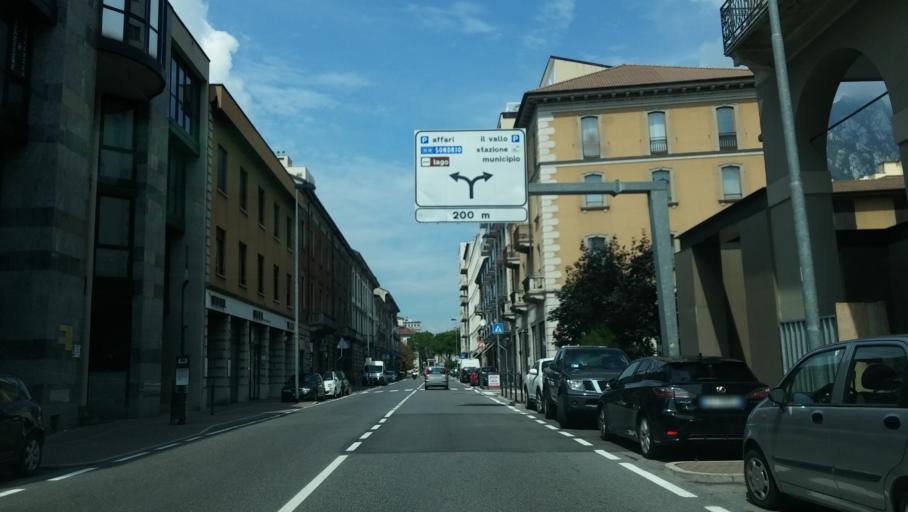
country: IT
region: Lombardy
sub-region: Provincia di Lecco
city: Lecco
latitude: 45.8502
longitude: 9.3940
